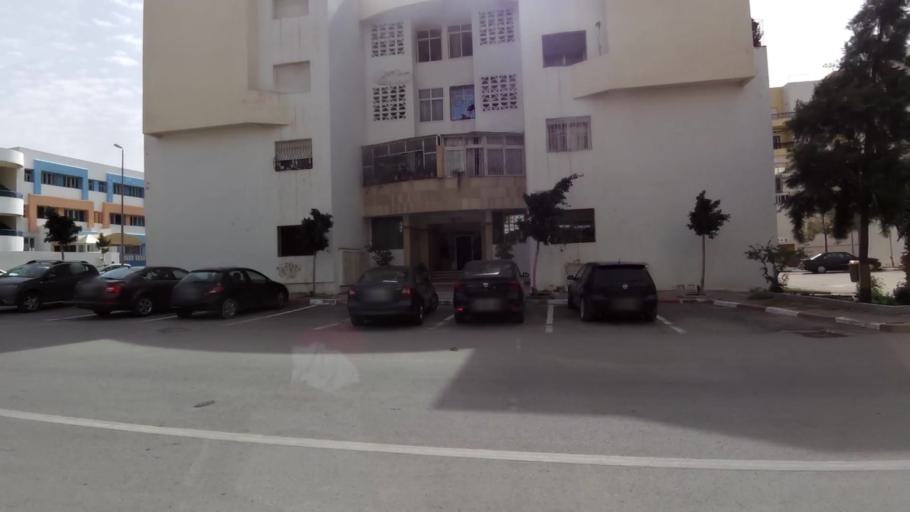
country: MA
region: Tanger-Tetouan
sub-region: Tanger-Assilah
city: Tangier
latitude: 35.7436
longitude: -5.8401
